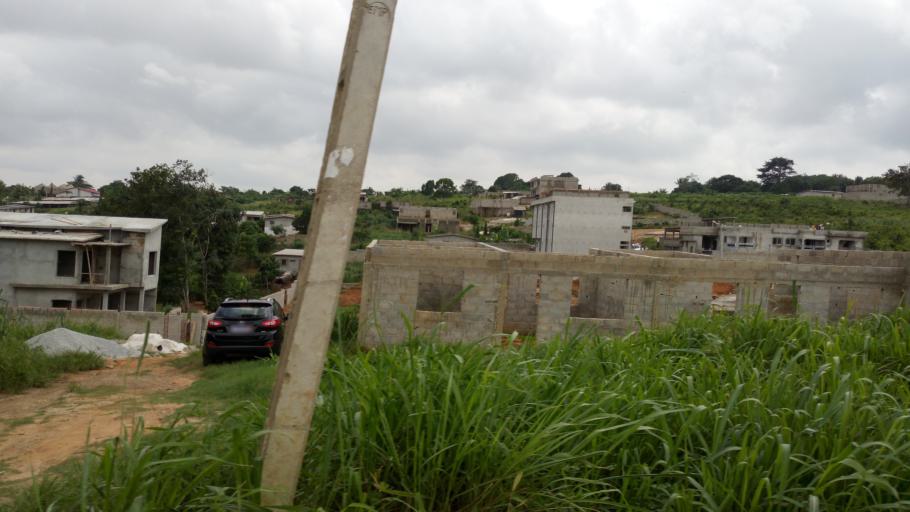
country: CI
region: Lagunes
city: Bingerville
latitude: 5.3576
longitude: -3.8908
